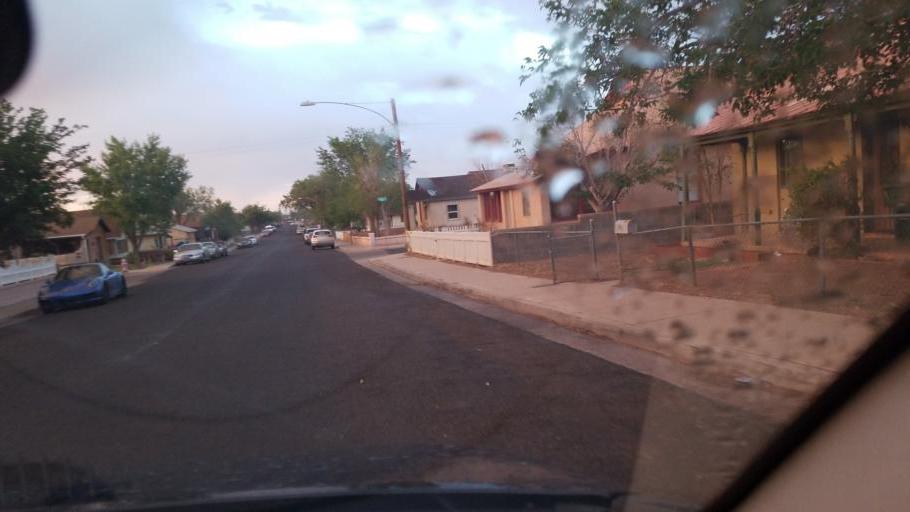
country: US
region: Arizona
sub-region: Navajo County
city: Winslow
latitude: 35.0265
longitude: -110.6962
